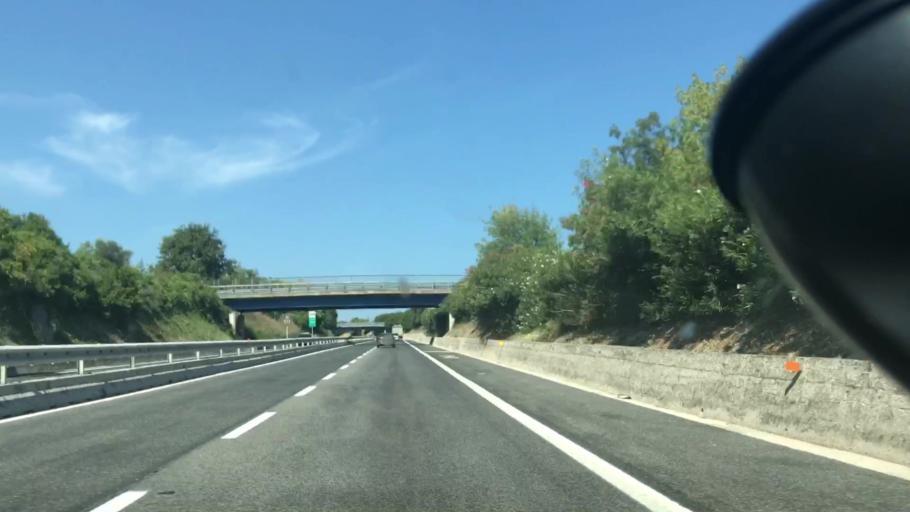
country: IT
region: Abruzzo
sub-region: Provincia di Chieti
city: Casalbordino-Miracoli
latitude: 42.1669
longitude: 14.6270
